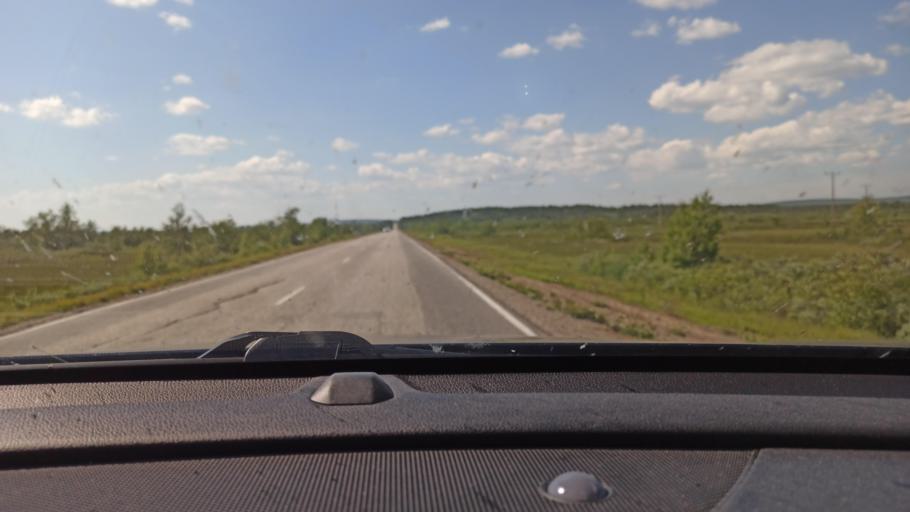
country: NO
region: Finnmark Fylke
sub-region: Kautokeino
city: Kautokeino
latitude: 68.4844
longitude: 22.2570
